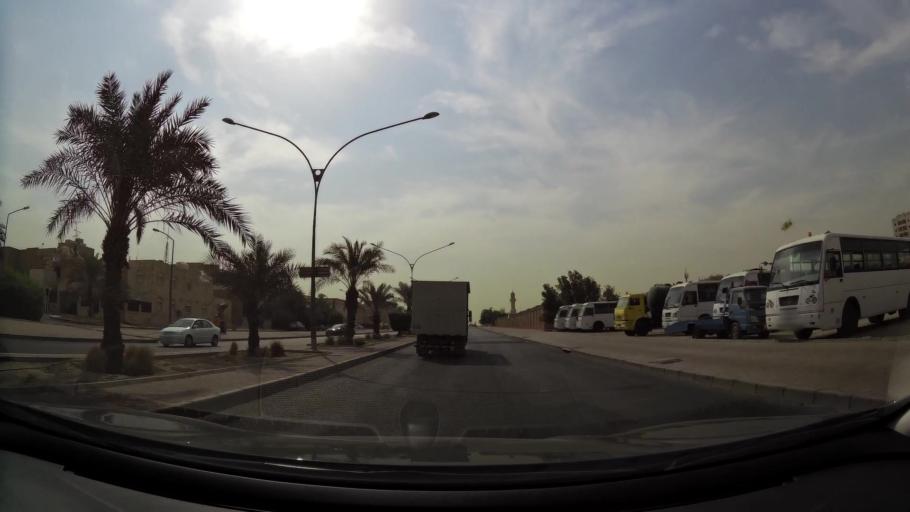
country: KW
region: Al Farwaniyah
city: Janub as Surrah
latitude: 29.2804
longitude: 47.9773
